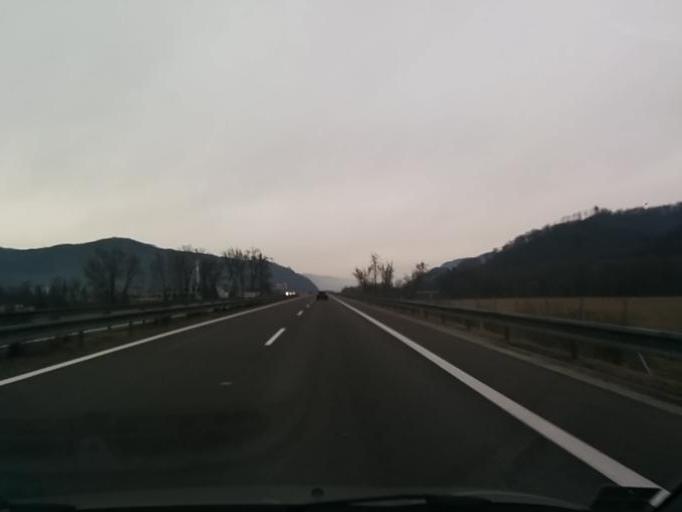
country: SK
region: Banskobystricky
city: Zarnovica
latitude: 48.4798
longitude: 18.7299
